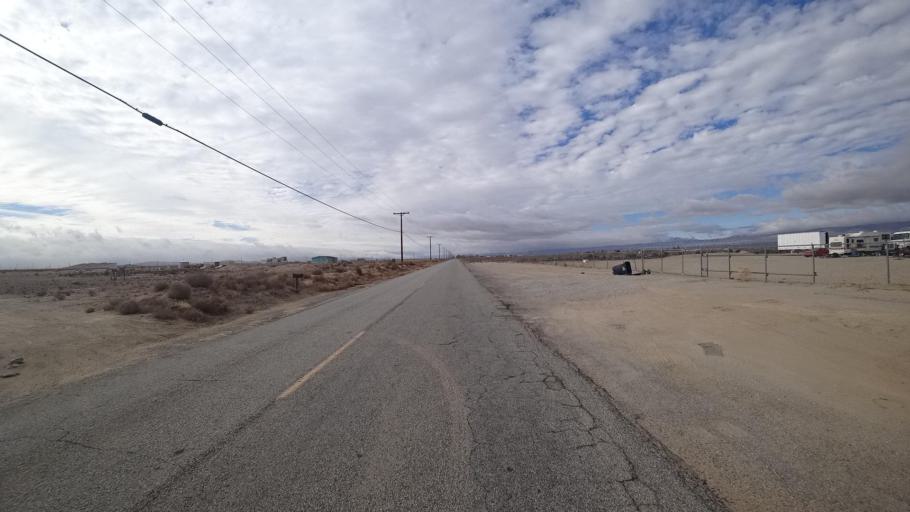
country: US
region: California
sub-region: Kern County
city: Rosamond
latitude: 34.8201
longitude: -118.2817
